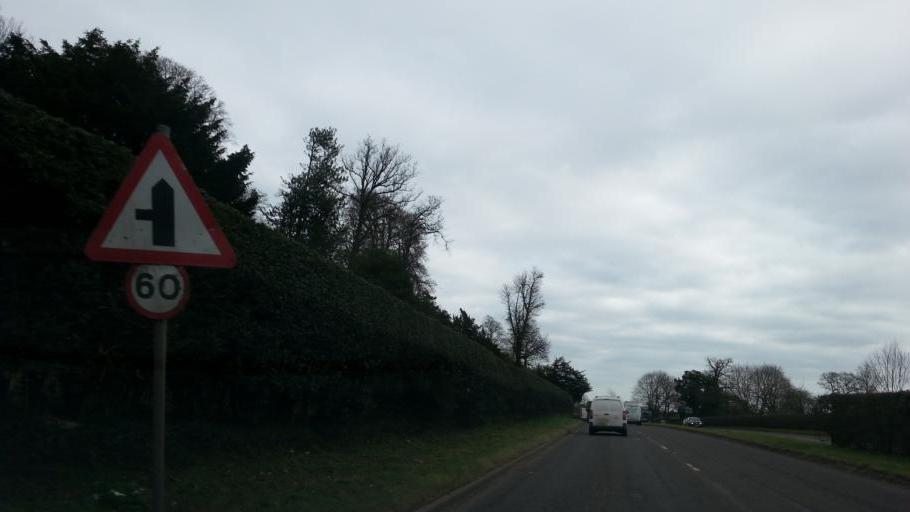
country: GB
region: England
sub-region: Staffordshire
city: Stafford
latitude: 52.8543
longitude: -2.0698
